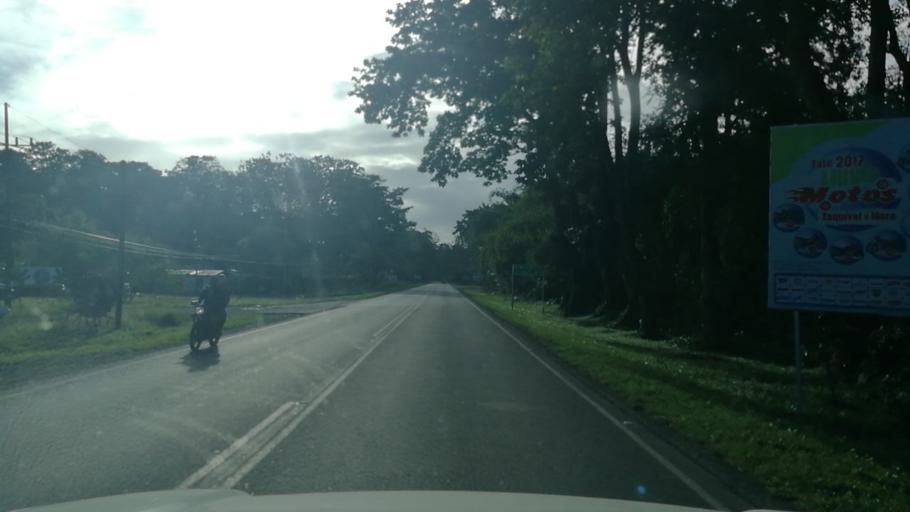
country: CR
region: Limon
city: Matina
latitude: 10.0349
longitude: -83.2671
